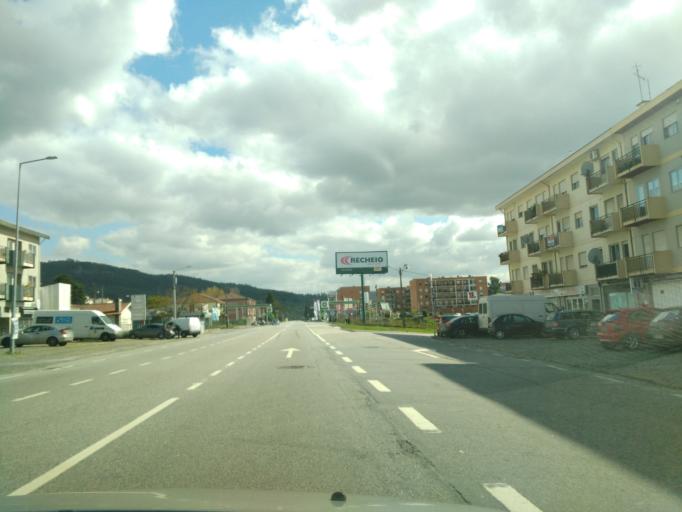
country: PT
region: Braga
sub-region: Braga
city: Braga
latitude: 41.5328
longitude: -8.4192
